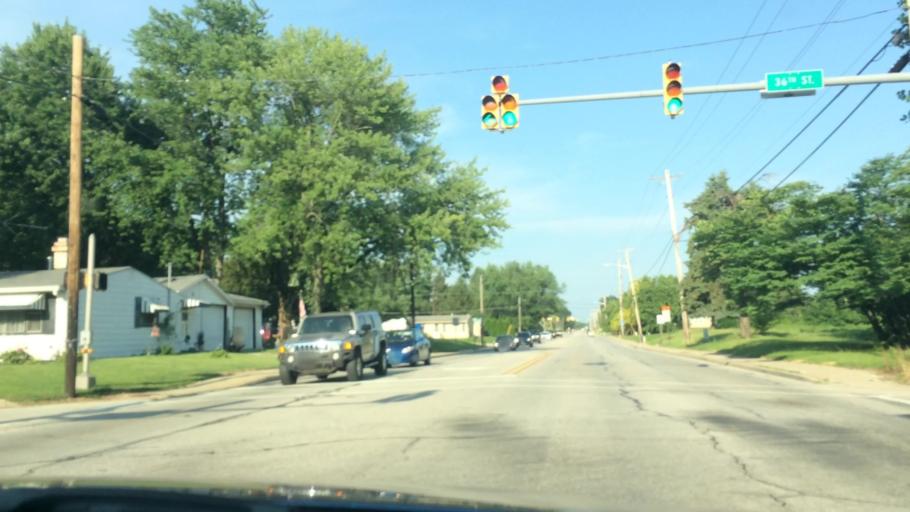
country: US
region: Indiana
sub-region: Tippecanoe County
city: Lafayette
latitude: 40.4249
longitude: -86.8506
